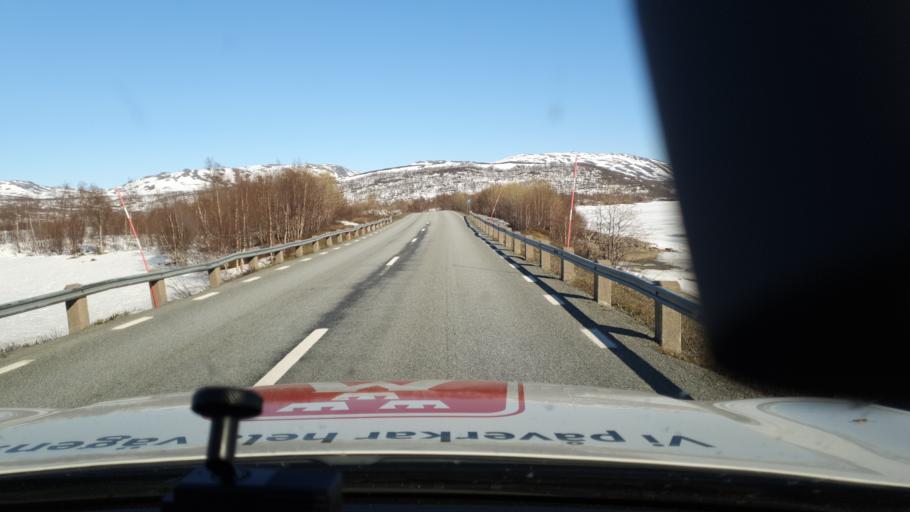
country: NO
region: Nordland
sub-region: Rana
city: Mo i Rana
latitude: 66.1219
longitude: 14.7896
